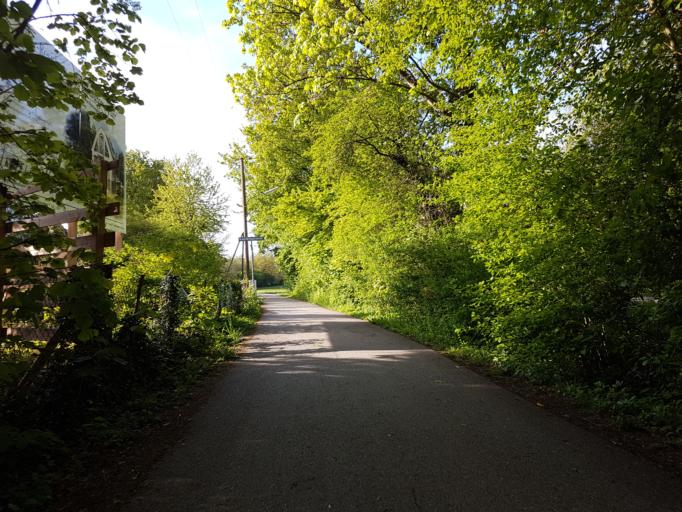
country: DE
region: Bavaria
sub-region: Upper Bavaria
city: Pasing
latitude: 48.1611
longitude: 11.4585
